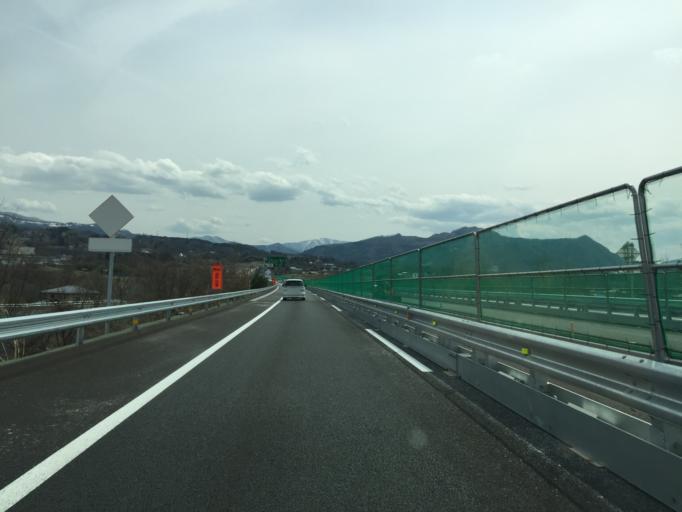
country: JP
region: Yamagata
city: Kaminoyama
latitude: 38.1906
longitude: 140.3008
